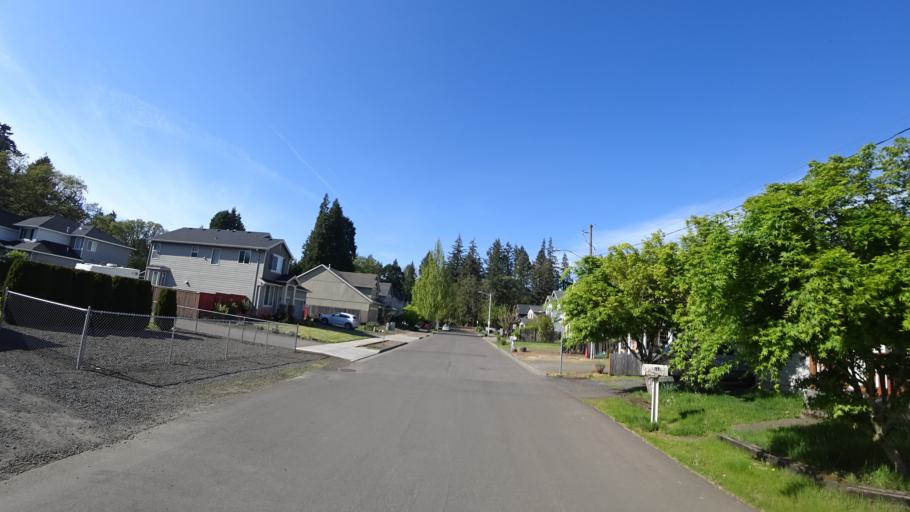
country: US
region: Oregon
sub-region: Washington County
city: Hillsboro
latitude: 45.5306
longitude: -122.9844
